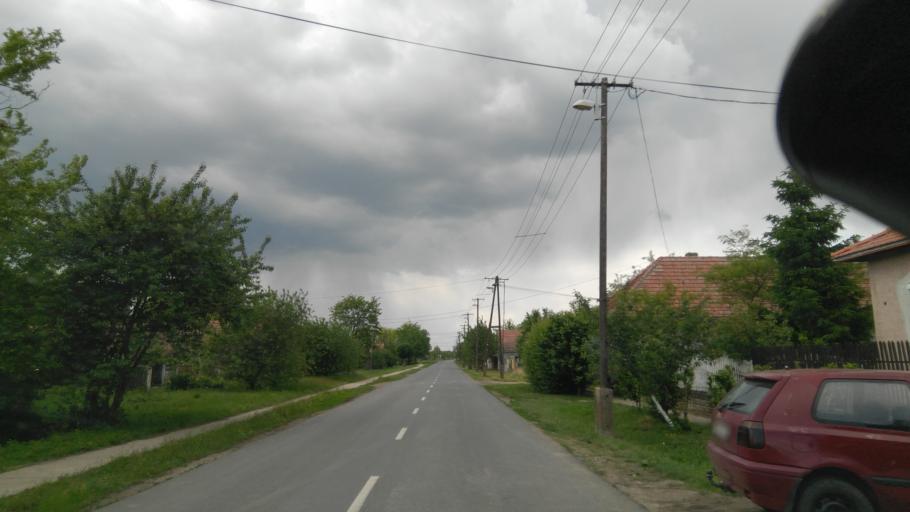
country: HU
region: Bekes
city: Dombegyhaz
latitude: 46.3482
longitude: 21.1222
